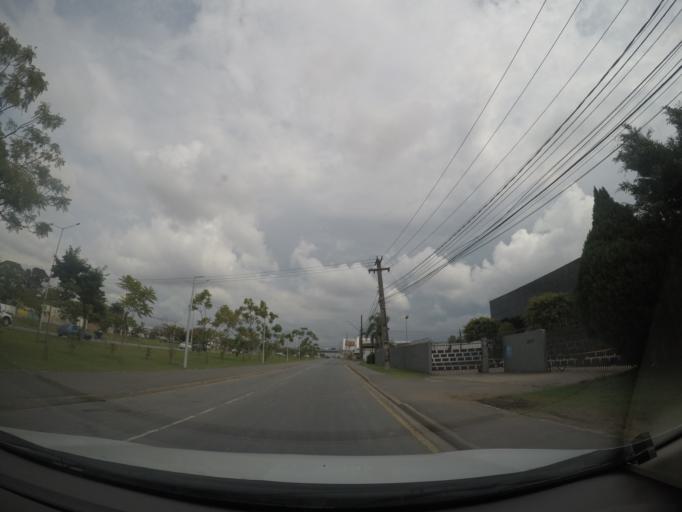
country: BR
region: Parana
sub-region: Curitiba
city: Curitiba
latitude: -25.4933
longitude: -49.2739
